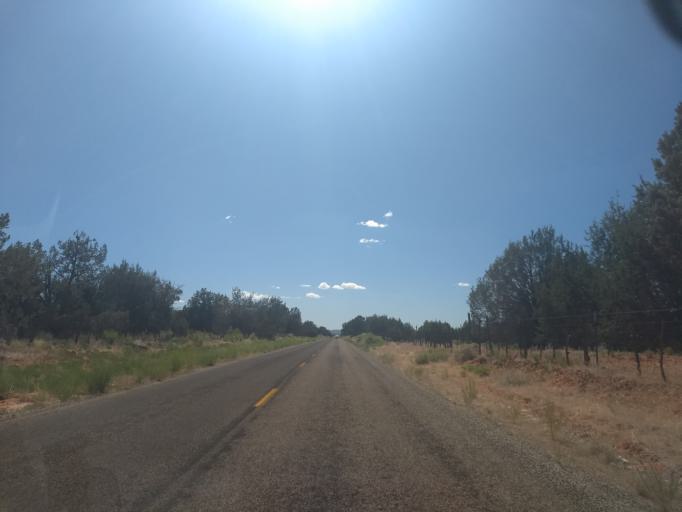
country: US
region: Utah
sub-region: Washington County
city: Hildale
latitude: 36.9468
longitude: -112.8802
